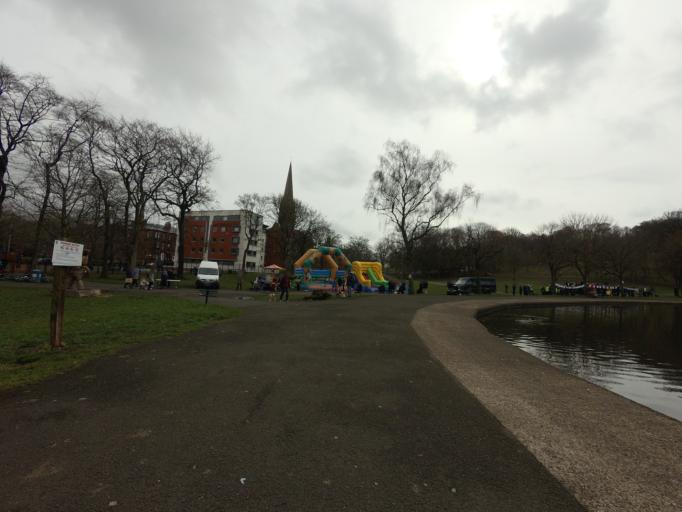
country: GB
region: Scotland
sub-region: Glasgow City
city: Glasgow
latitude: 55.8344
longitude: -4.2730
